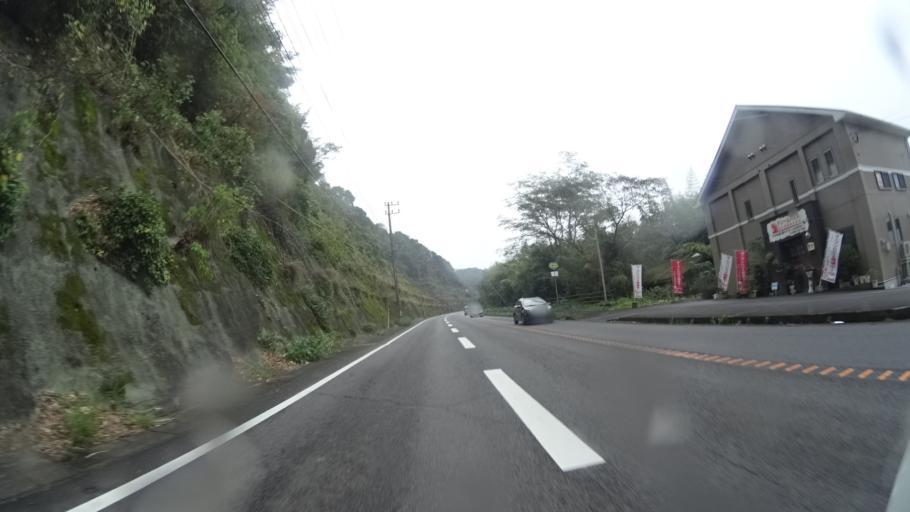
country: JP
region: Kagoshima
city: Kajiki
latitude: 31.7502
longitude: 130.6721
